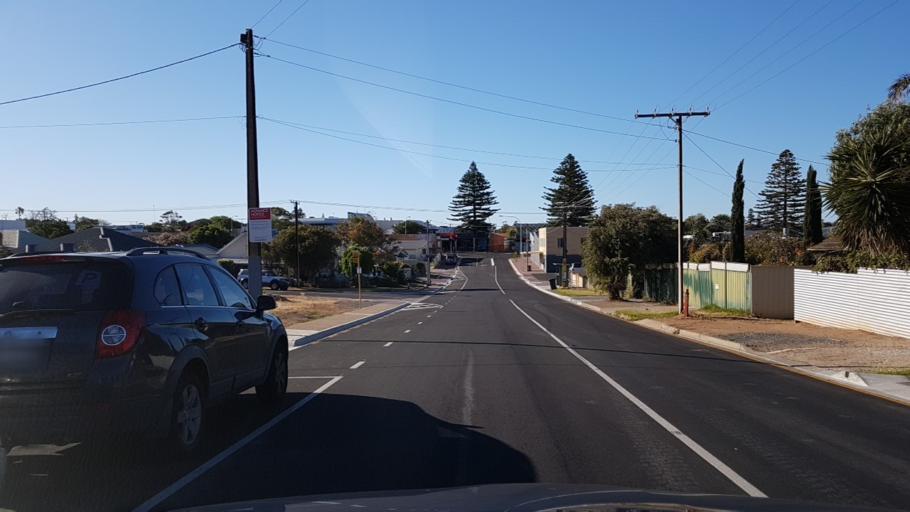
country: AU
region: South Australia
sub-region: Adelaide
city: Port Noarlunga
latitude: -35.1378
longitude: 138.4737
